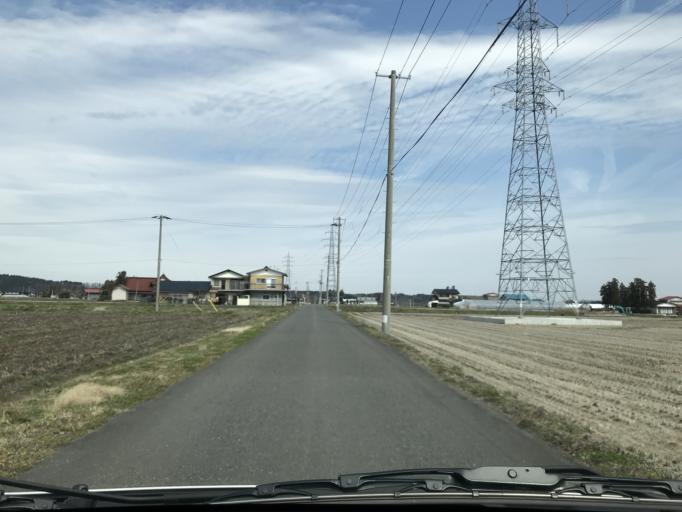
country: JP
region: Iwate
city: Mizusawa
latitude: 39.1477
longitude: 141.0818
